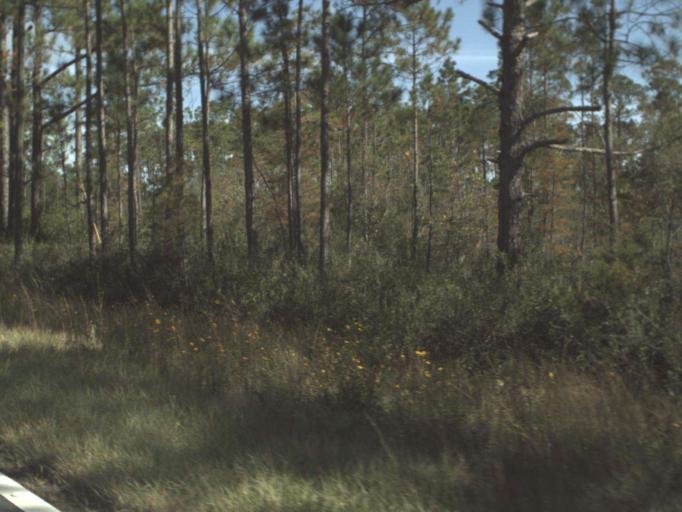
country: US
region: Florida
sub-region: Gulf County
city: Wewahitchka
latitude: 30.0808
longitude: -84.9833
